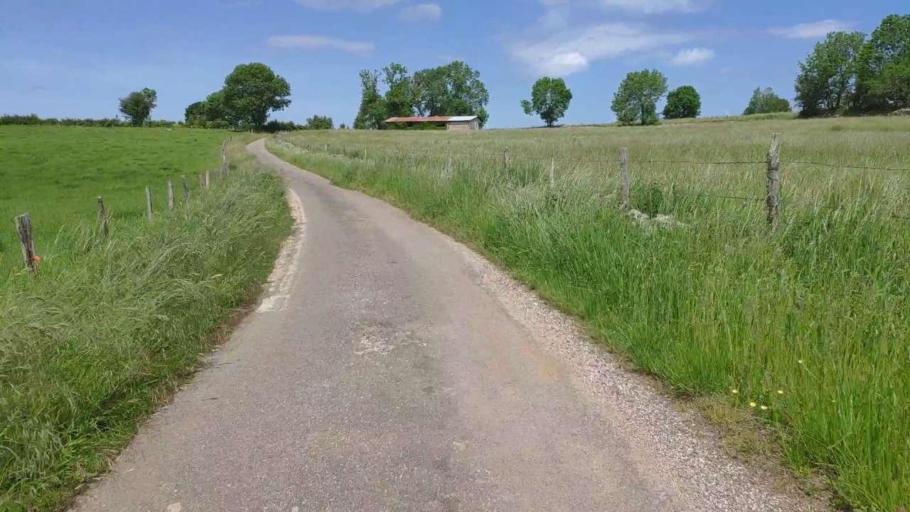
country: FR
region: Franche-Comte
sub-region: Departement du Jura
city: Perrigny
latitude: 46.7495
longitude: 5.6374
